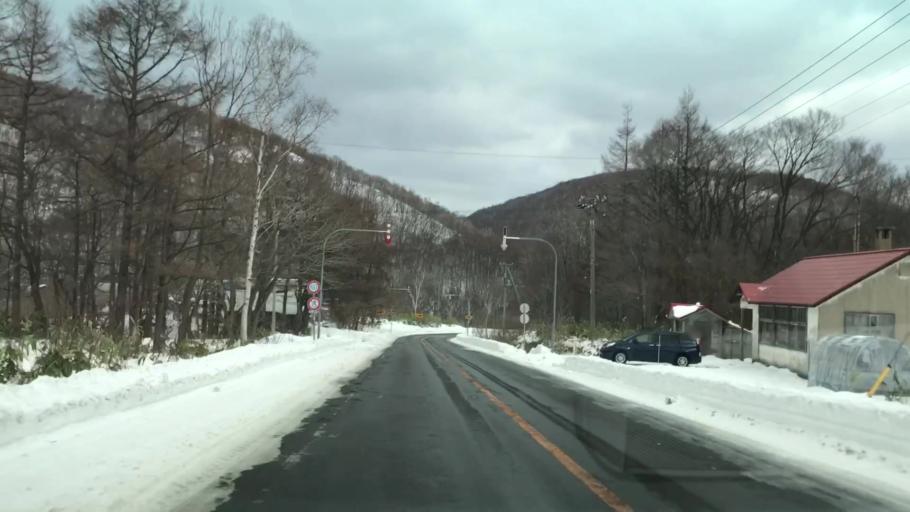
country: JP
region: Hokkaido
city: Yoichi
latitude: 43.3251
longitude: 140.5090
